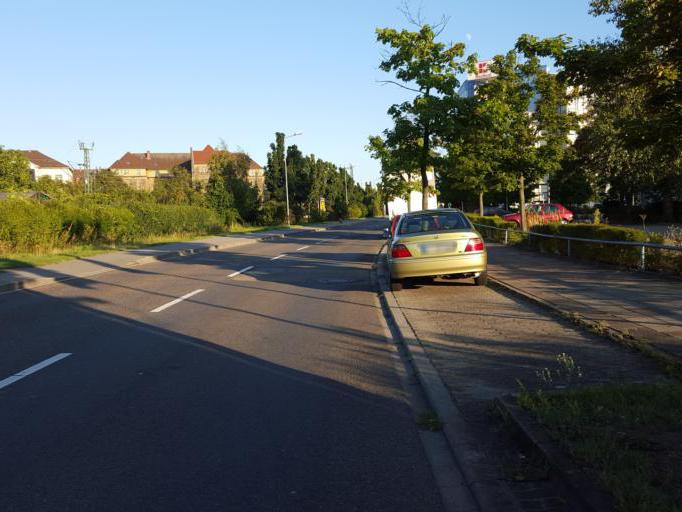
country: DE
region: Baden-Wuerttemberg
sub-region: Karlsruhe Region
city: Karlsruhe
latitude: 49.0115
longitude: 8.3524
